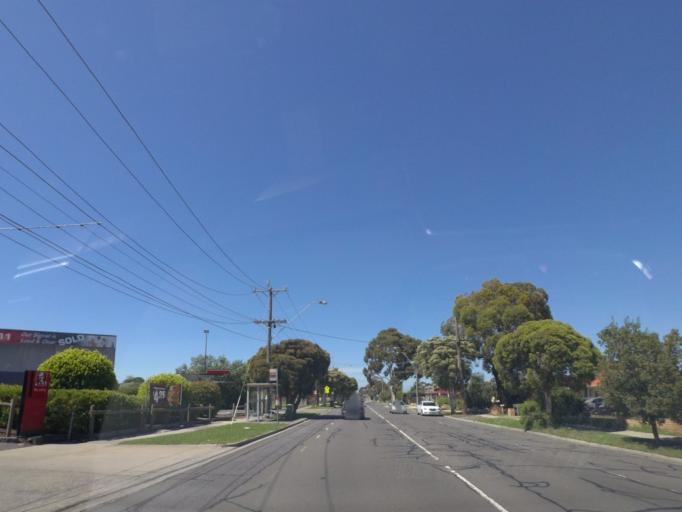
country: AU
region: Victoria
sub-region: Hume
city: Tullamarine
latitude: -37.7004
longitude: 144.8801
